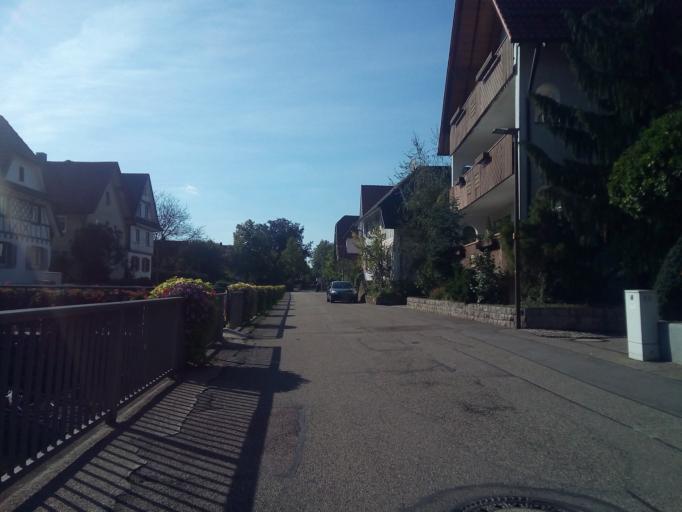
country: DE
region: Baden-Wuerttemberg
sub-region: Freiburg Region
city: Sasbach
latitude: 48.6398
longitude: 8.0954
